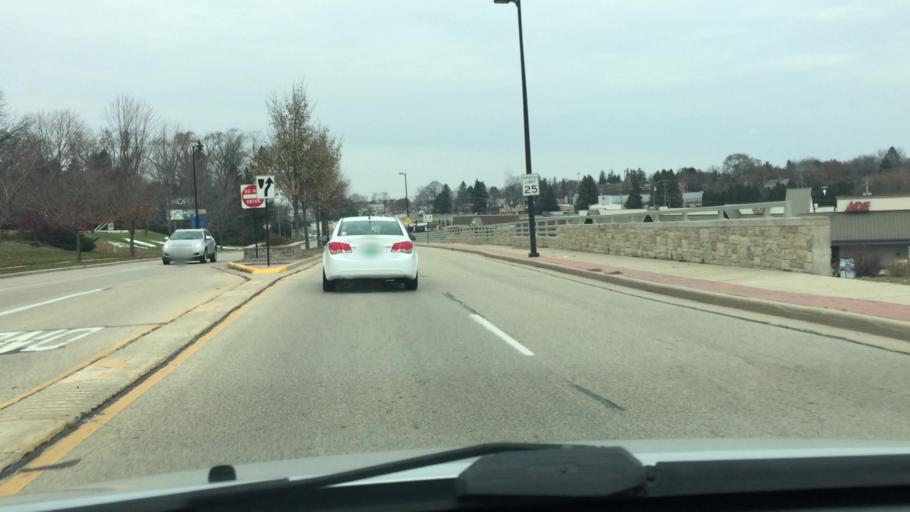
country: US
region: Wisconsin
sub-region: Ozaukee County
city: Grafton
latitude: 43.3089
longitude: -87.9582
